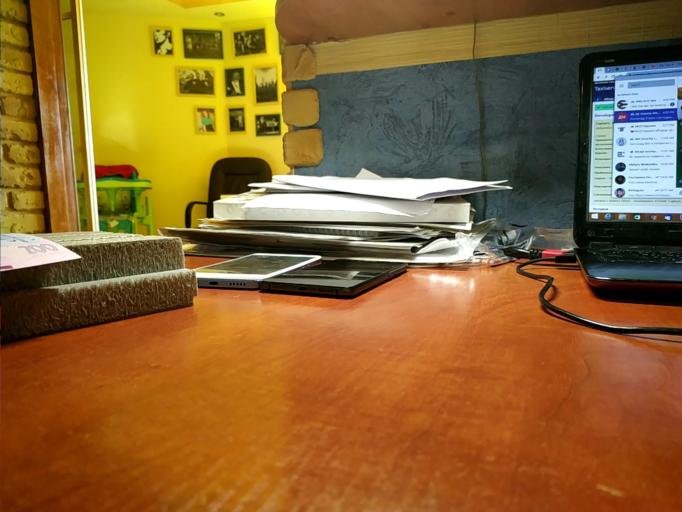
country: RU
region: Vologda
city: Nelazskoye
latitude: 59.4394
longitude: 37.6072
